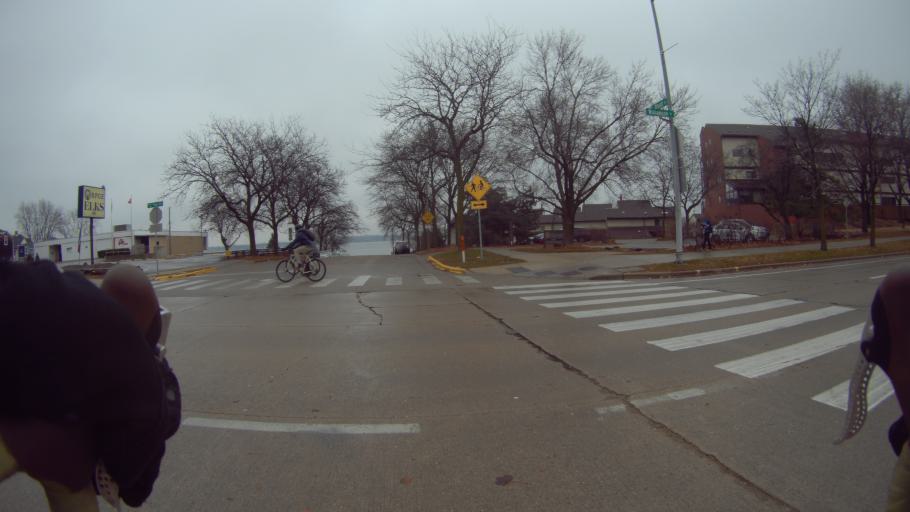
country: US
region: Wisconsin
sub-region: Dane County
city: Madison
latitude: 43.0775
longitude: -89.3735
